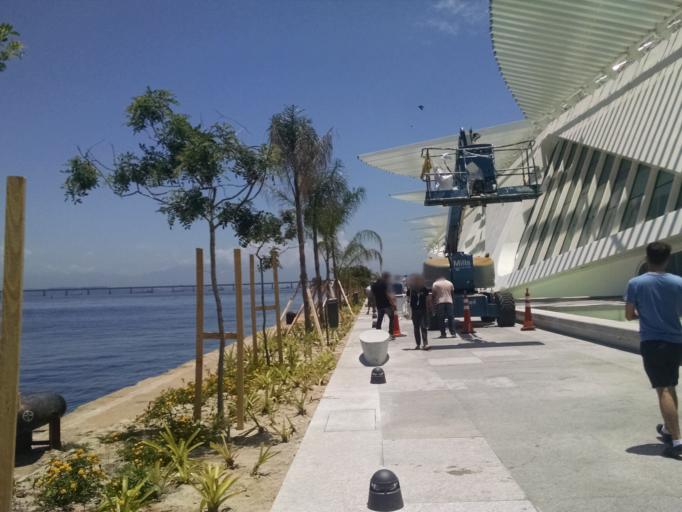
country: BR
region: Rio de Janeiro
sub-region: Rio De Janeiro
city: Rio de Janeiro
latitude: -22.8948
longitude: -43.1800
